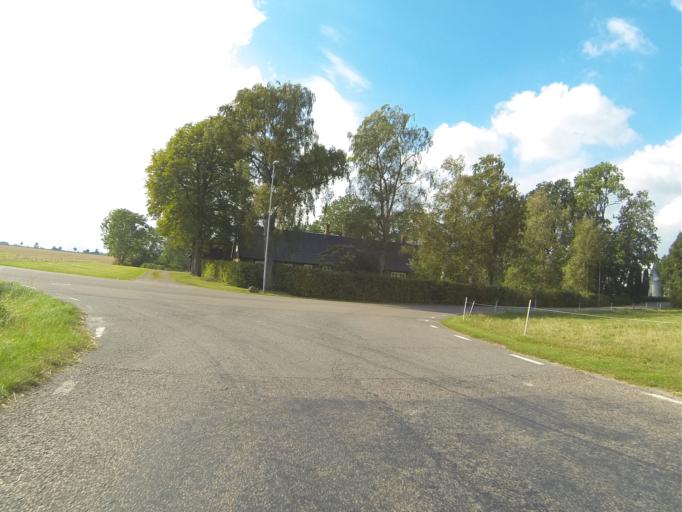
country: SE
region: Skane
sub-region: Lunds Kommun
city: Lund
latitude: 55.7639
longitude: 13.1731
